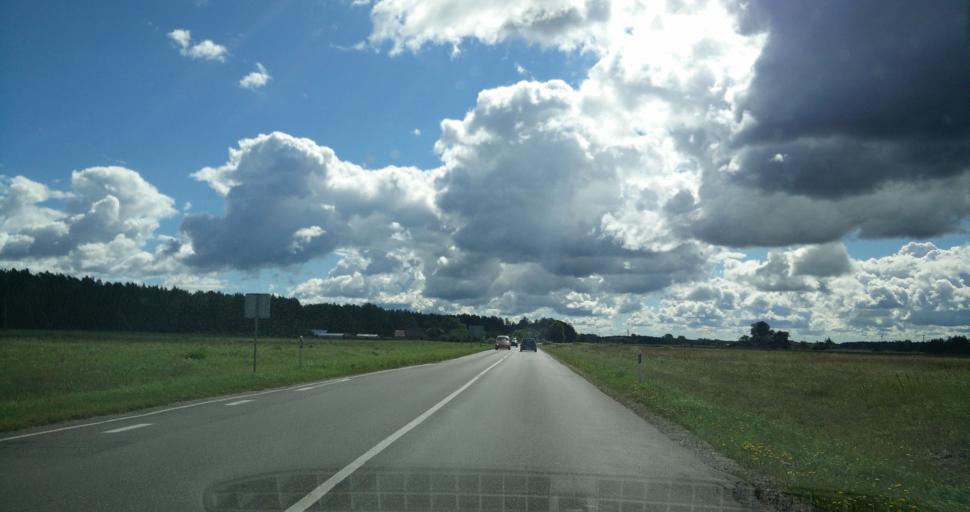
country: LT
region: Klaipedos apskritis
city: Silute
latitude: 55.3308
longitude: 21.5169
